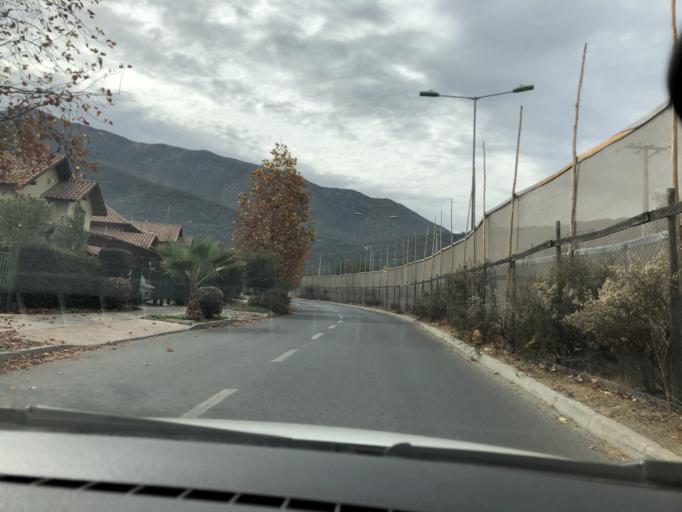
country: CL
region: Santiago Metropolitan
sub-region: Provincia de Cordillera
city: Puente Alto
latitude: -33.5872
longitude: -70.5086
